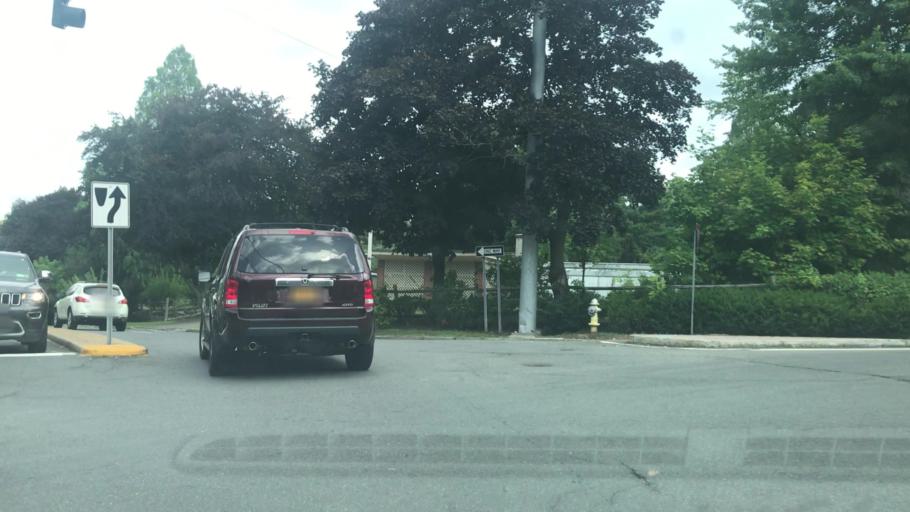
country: US
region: New York
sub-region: Westchester County
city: Tuckahoe
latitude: 40.9545
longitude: -73.7969
